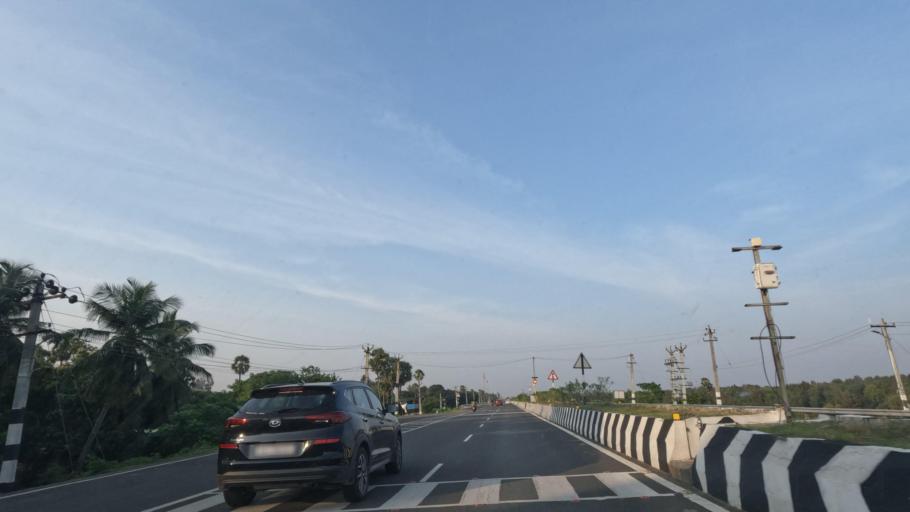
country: IN
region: Tamil Nadu
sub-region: Kancheepuram
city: Mamallapuram
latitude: 12.7186
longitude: 80.2281
